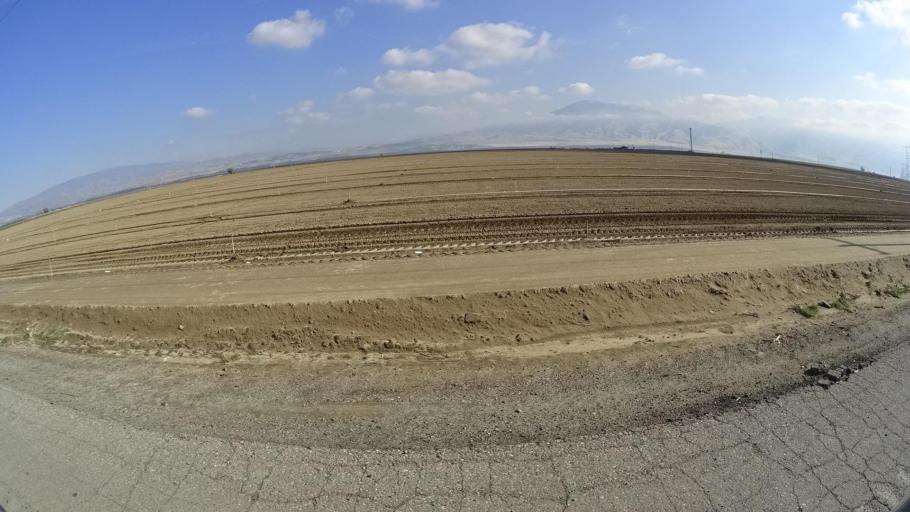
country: US
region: California
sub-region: Kern County
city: Arvin
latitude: 35.2558
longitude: -118.8247
